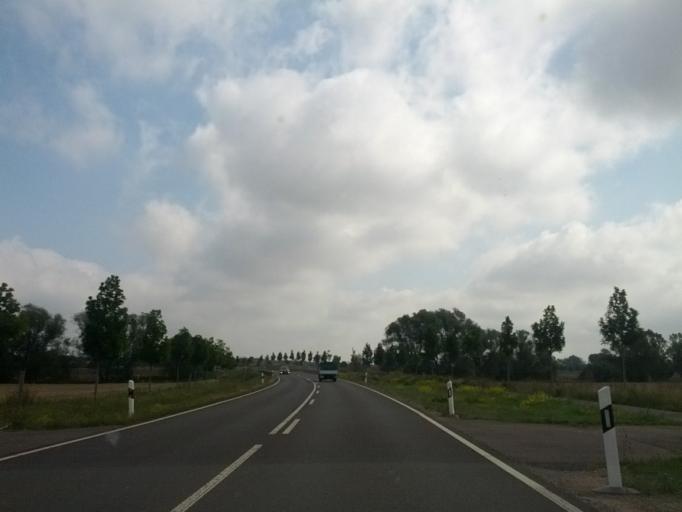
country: DE
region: Thuringia
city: Emleben
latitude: 50.9238
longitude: 10.6943
